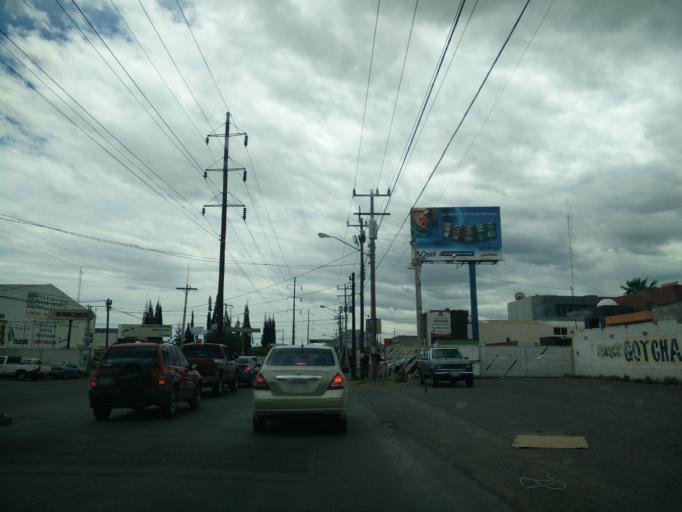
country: MX
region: Chihuahua
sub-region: Chihuahua
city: Chihuahua
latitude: 28.6696
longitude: -106.0852
